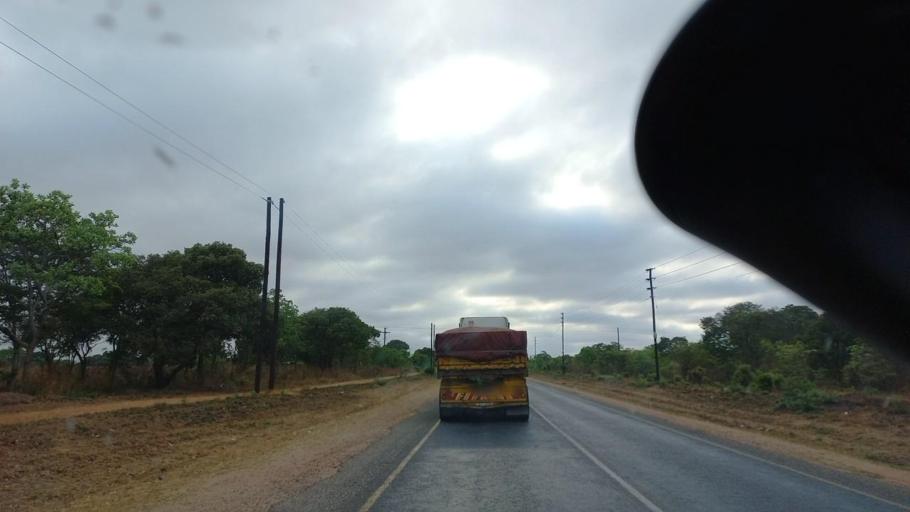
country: ZM
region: Lusaka
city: Chongwe
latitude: -15.3527
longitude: 28.5439
